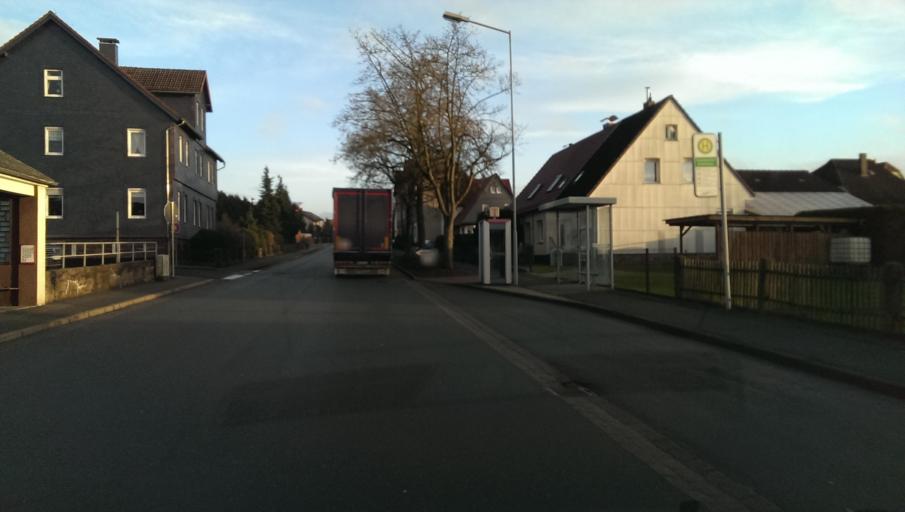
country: DE
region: Lower Saxony
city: Stadtoldendorf
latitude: 51.8820
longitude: 9.6351
